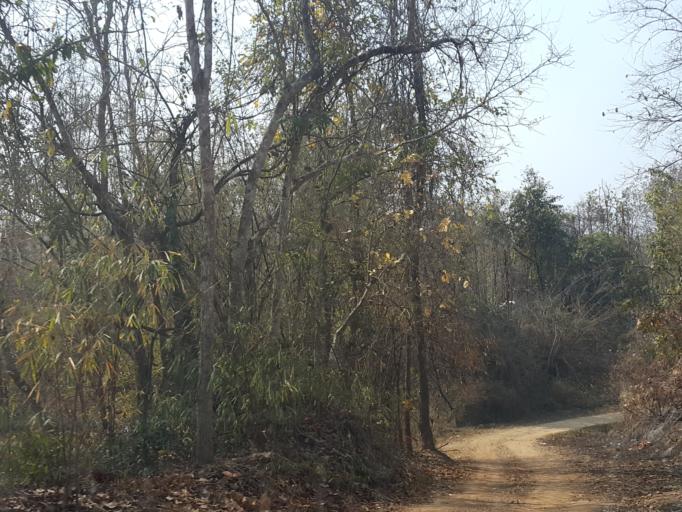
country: TH
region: Chiang Mai
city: Hang Dong
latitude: 18.7188
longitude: 98.8567
